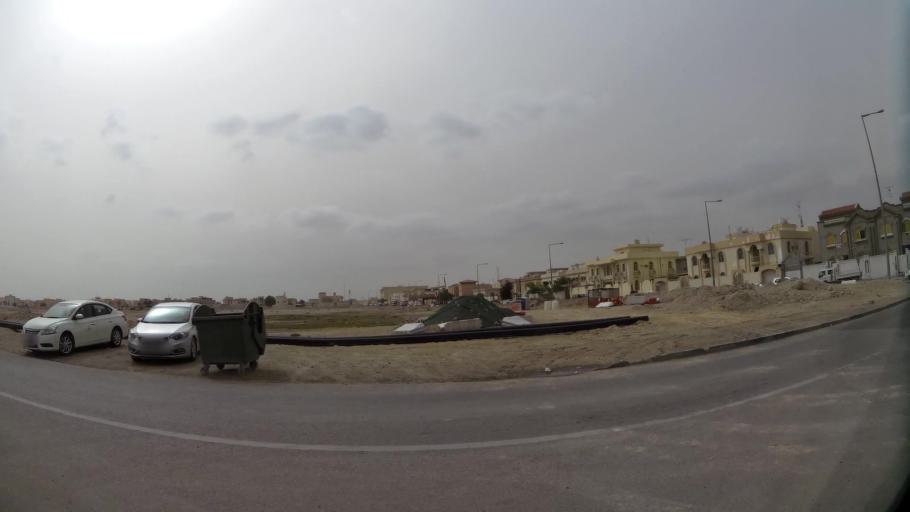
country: QA
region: Baladiyat ad Dawhah
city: Doha
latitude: 25.2457
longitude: 51.5302
